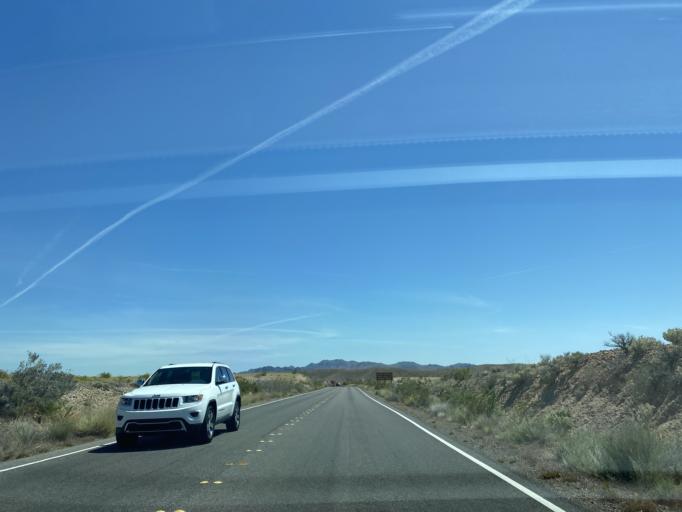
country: US
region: Nevada
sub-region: Clark County
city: Henderson
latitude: 36.1704
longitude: -114.9123
